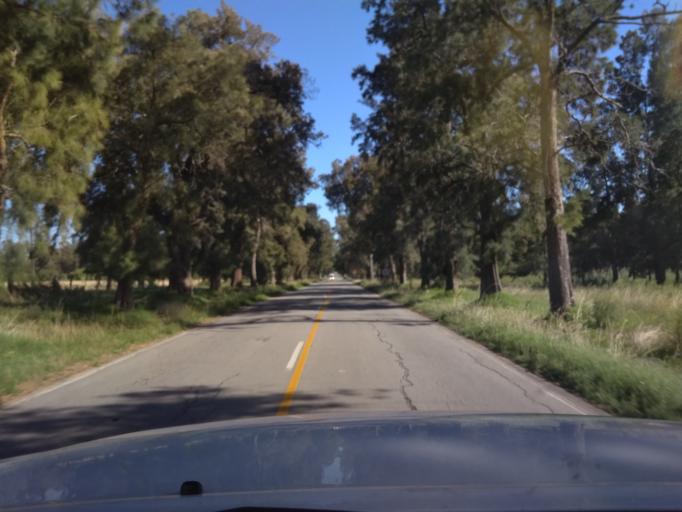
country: UY
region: Canelones
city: San Bautista
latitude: -34.3827
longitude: -55.9595
